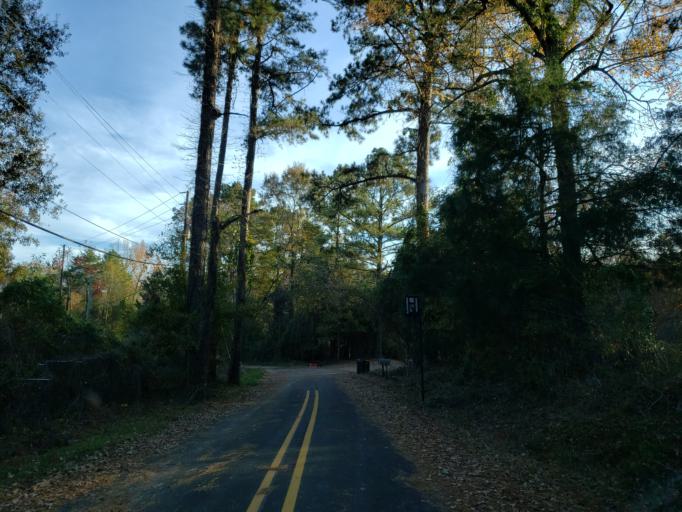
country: US
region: Mississippi
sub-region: Lamar County
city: Arnold Line
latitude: 31.3483
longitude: -89.3532
